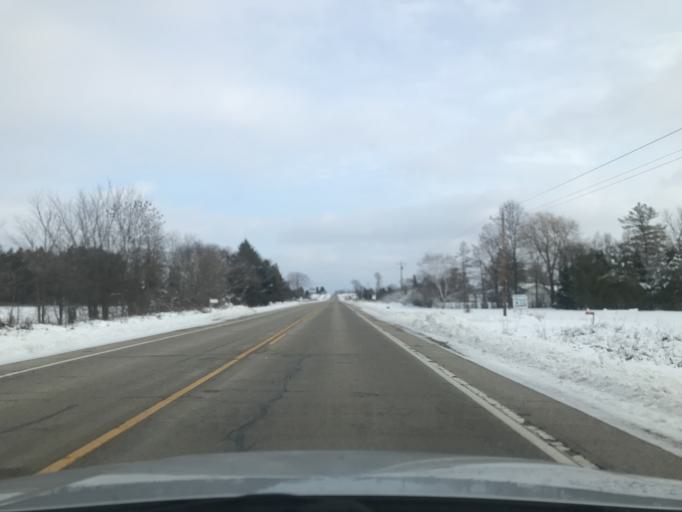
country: US
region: Wisconsin
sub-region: Oconto County
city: Oconto
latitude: 44.8935
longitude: -87.9965
